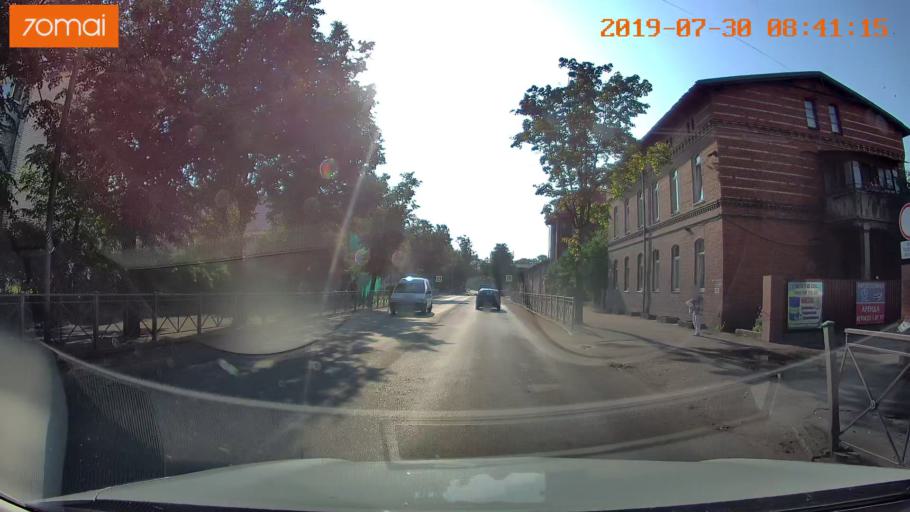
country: RU
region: Kaliningrad
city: Chernyakhovsk
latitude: 54.6306
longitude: 21.8159
